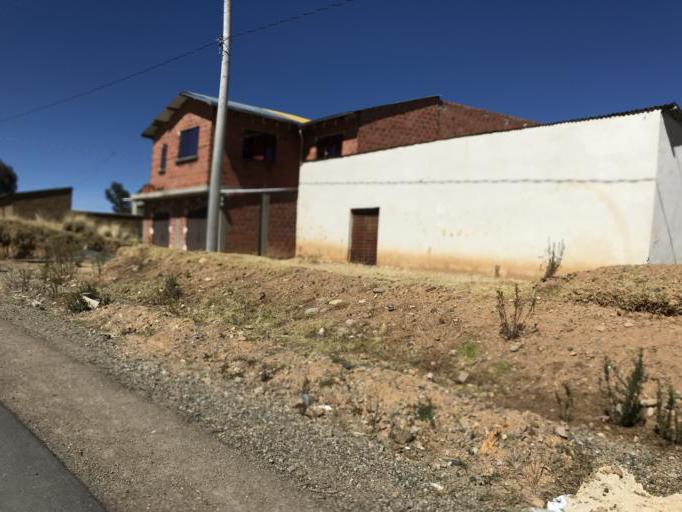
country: BO
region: La Paz
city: Huatajata
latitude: -16.2142
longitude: -68.6594
